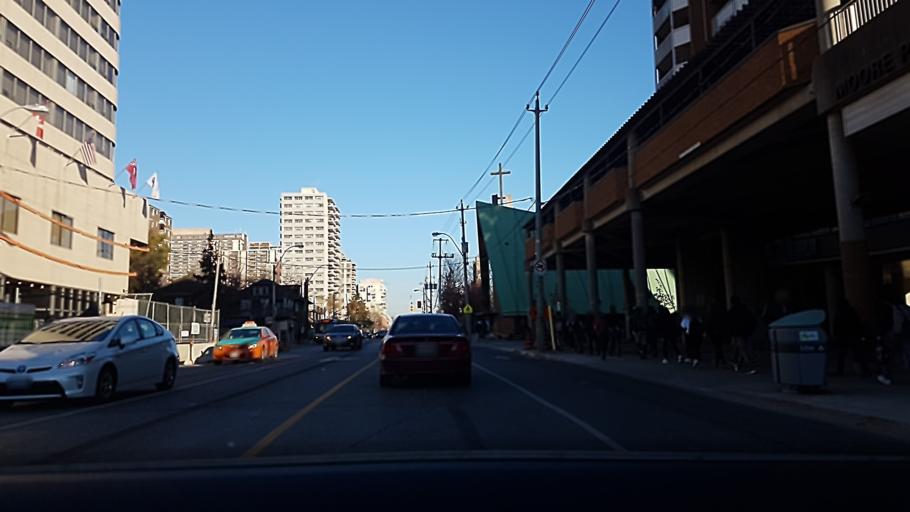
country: CA
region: Ontario
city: Toronto
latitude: 43.7085
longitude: -79.3902
